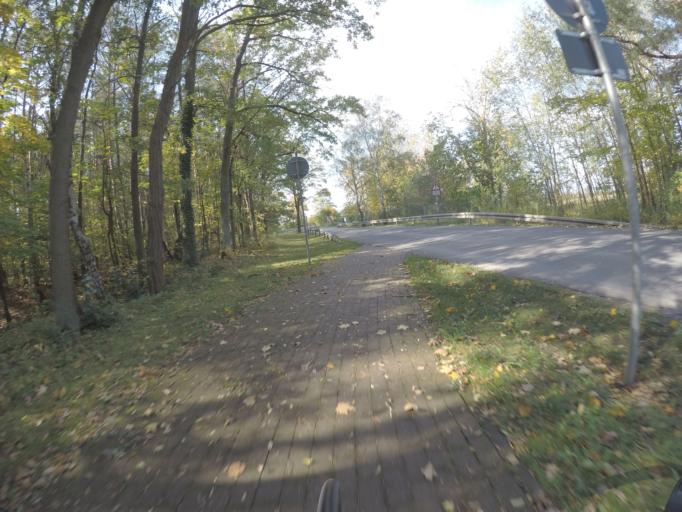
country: DE
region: Brandenburg
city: Hohen Neuendorf
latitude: 52.7031
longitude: 13.2424
